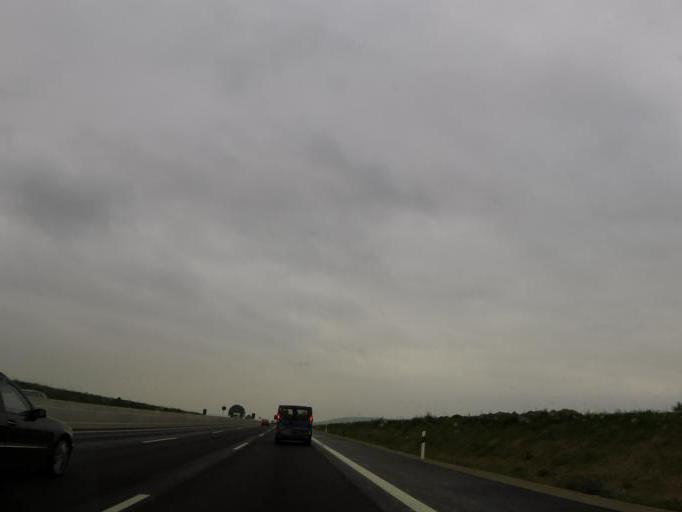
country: DE
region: Lower Saxony
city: Seesen
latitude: 51.9111
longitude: 10.1341
